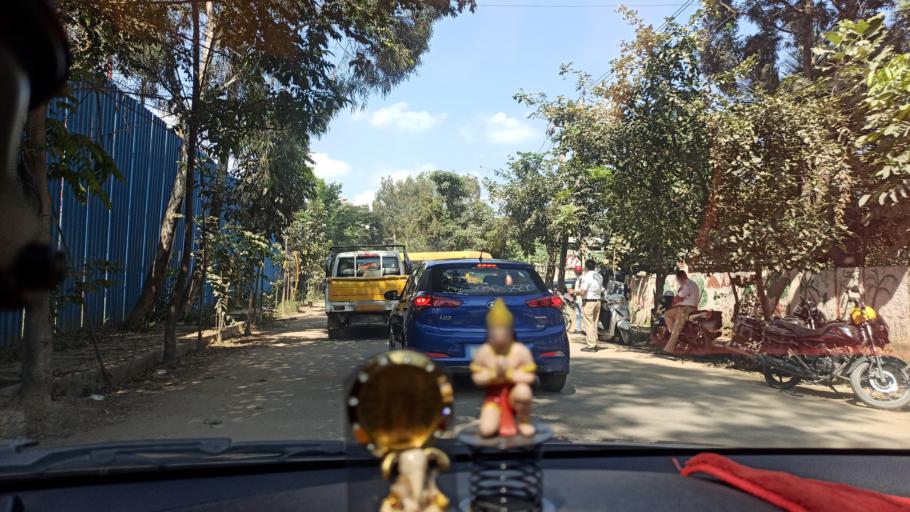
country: IN
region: Karnataka
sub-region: Bangalore Urban
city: Bangalore
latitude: 12.9731
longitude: 77.7076
